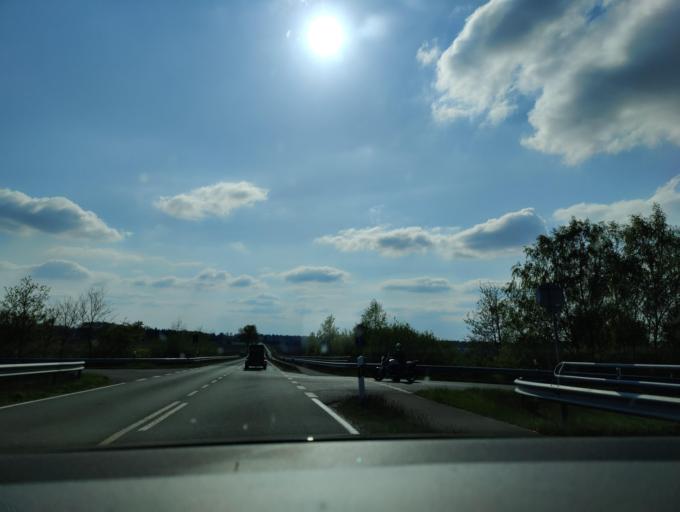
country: DE
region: Lower Saxony
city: Emsburen
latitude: 52.3787
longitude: 7.2441
